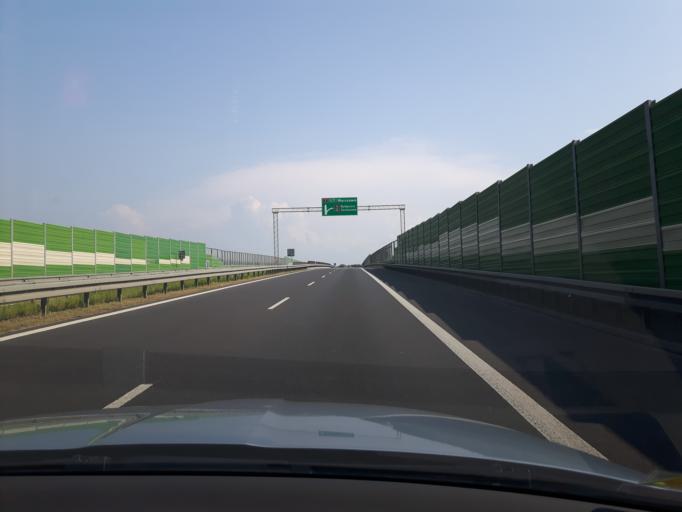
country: PL
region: Masovian Voivodeship
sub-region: Powiat plonski
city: Plonsk
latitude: 52.6068
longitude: 20.3984
